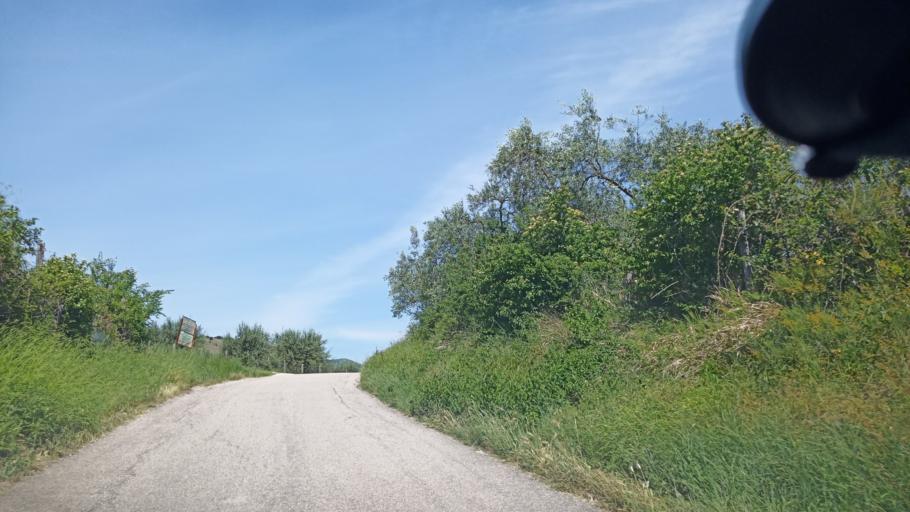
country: IT
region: Latium
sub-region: Provincia di Rieti
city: Torri in Sabina
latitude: 42.3560
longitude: 12.6347
